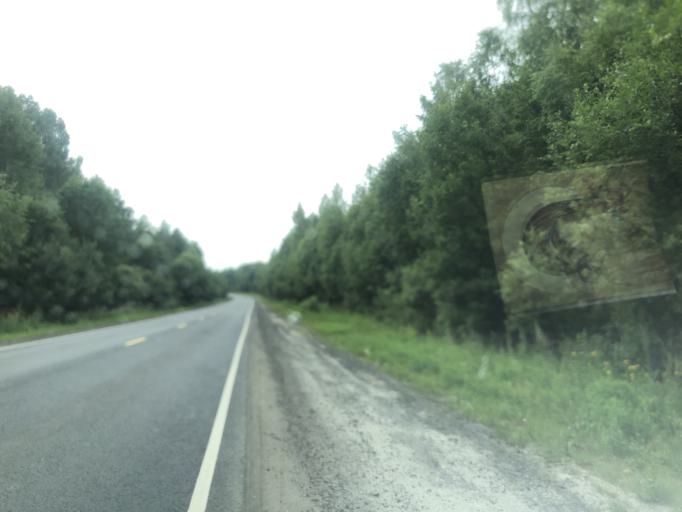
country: RU
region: Ivanovo
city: Verkhniy Landekh
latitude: 56.7798
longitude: 42.3711
